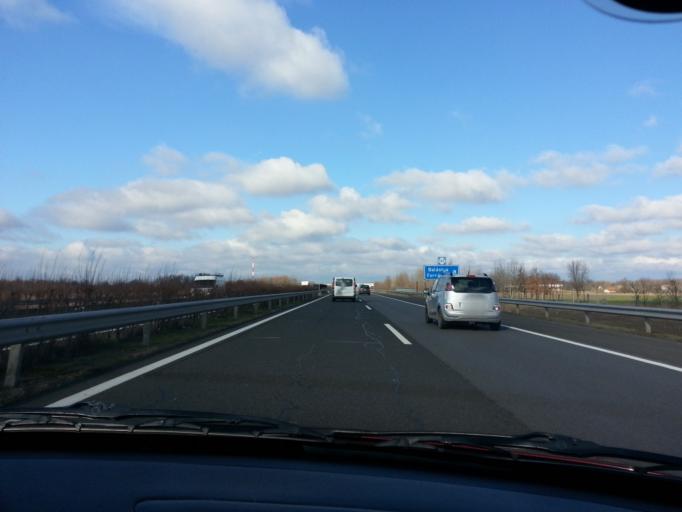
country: HU
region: Csongrad
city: Balastya
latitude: 46.3982
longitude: 19.9782
